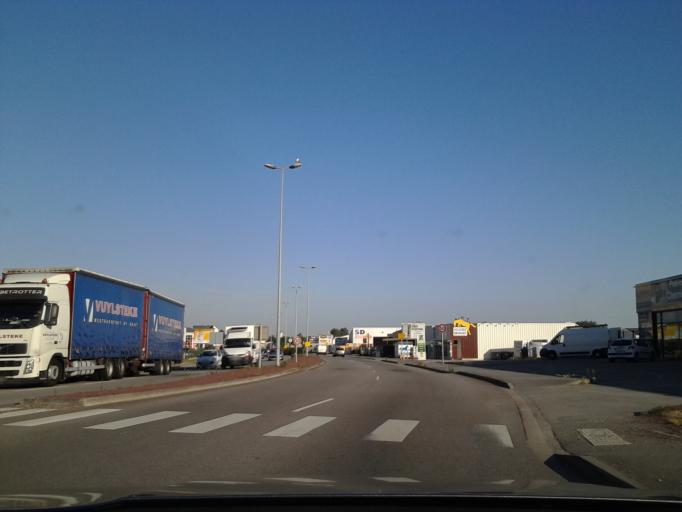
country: FR
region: Lower Normandy
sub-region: Departement de la Manche
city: Cherbourg-Octeville
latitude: 49.6354
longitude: -1.5917
